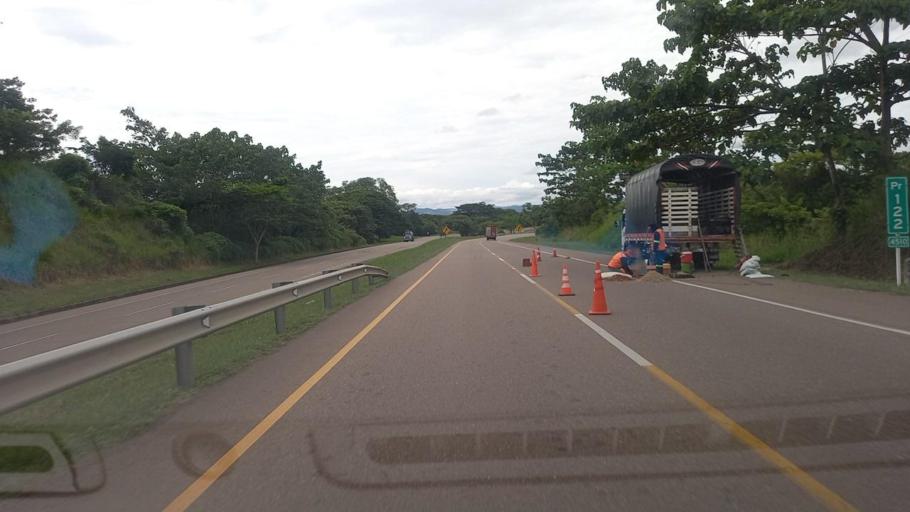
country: CO
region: Boyaca
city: Puerto Boyaca
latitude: 6.1529
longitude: -74.5720
